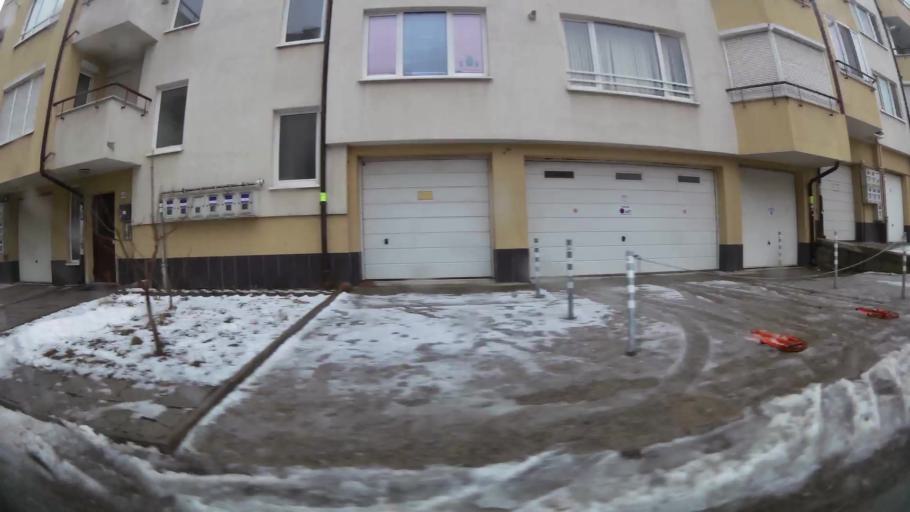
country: BG
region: Sofia-Capital
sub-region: Stolichna Obshtina
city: Sofia
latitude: 42.6609
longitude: 23.2914
